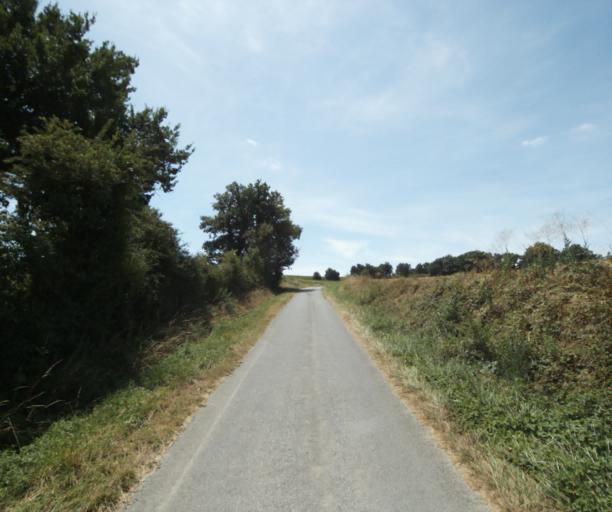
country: FR
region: Midi-Pyrenees
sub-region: Departement du Tarn
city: Soreze
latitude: 43.4946
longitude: 2.0626
